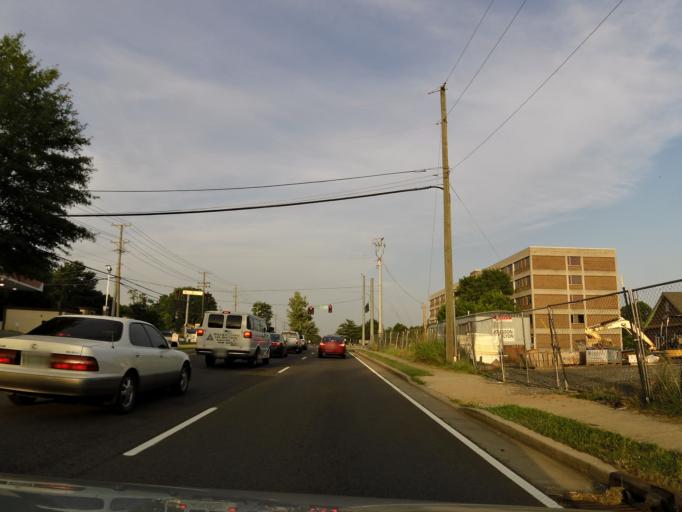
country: US
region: Tennessee
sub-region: Blount County
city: Louisville
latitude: 35.9415
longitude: -84.0429
